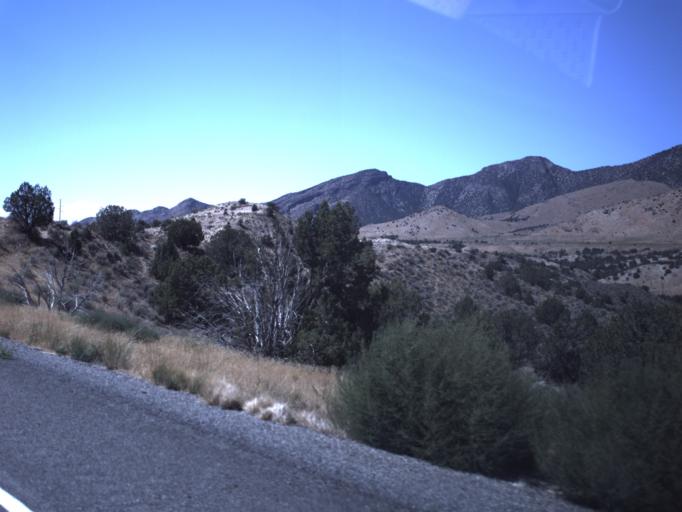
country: US
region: Utah
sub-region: Juab County
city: Nephi
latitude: 39.5745
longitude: -112.1856
